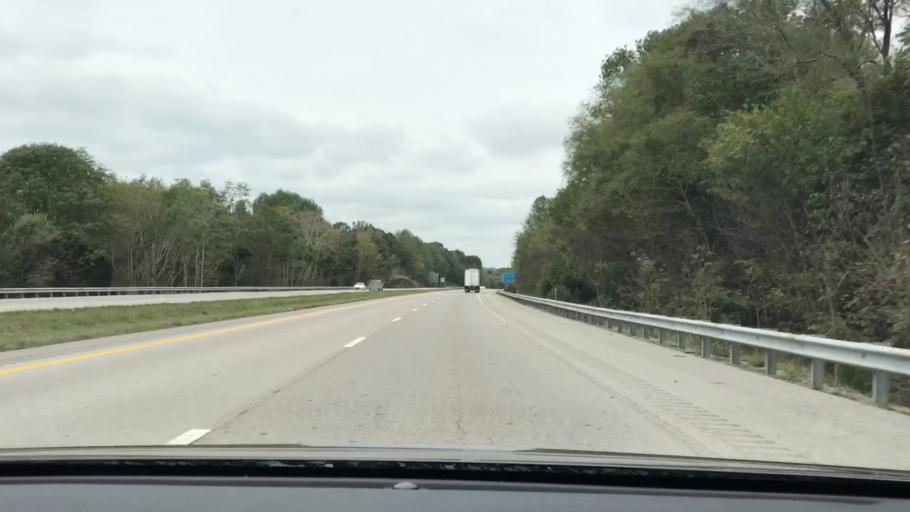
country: US
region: Kentucky
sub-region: Metcalfe County
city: Edmonton
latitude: 36.9984
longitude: -85.6261
